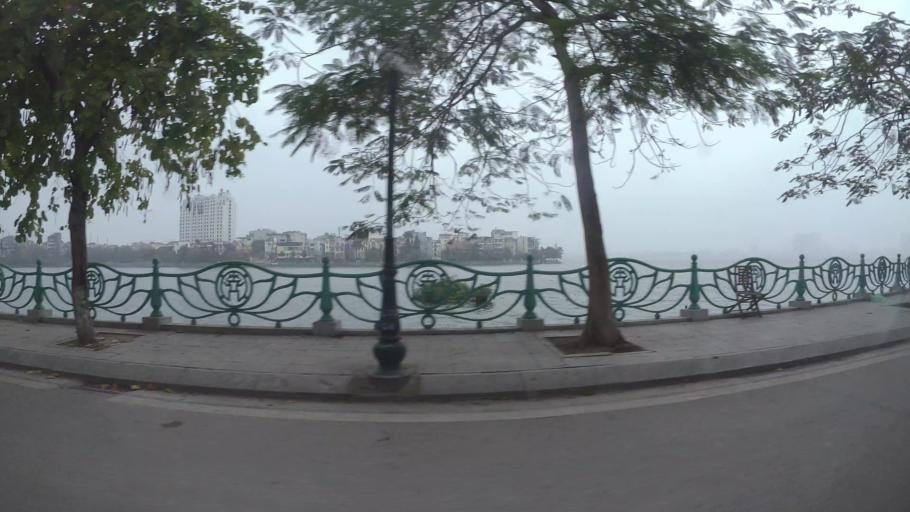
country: VN
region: Ha Noi
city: Tay Ho
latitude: 21.0608
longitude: 105.8276
